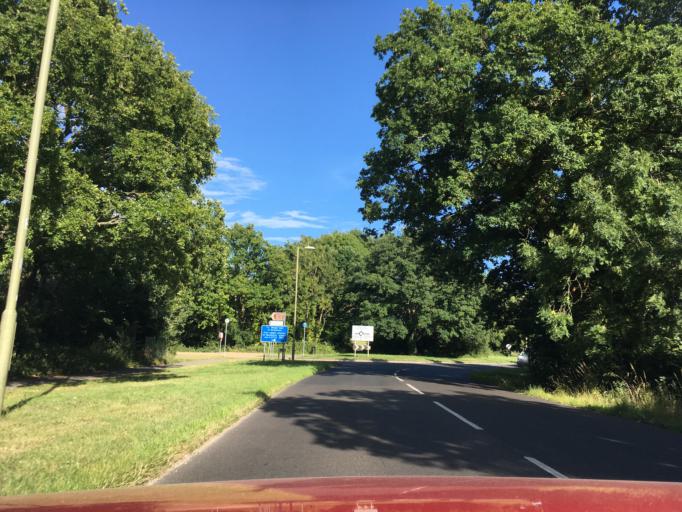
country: GB
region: England
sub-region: Hampshire
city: Romsey
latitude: 50.9856
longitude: -1.4638
